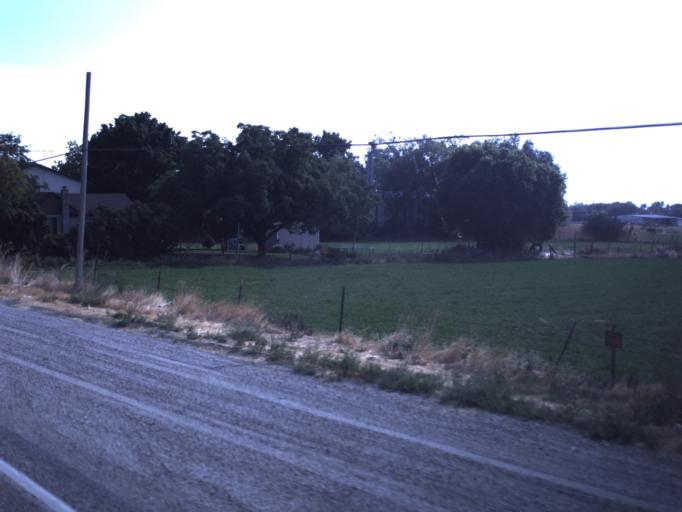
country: US
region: Utah
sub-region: Box Elder County
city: Willard
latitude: 41.4258
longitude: -112.0358
